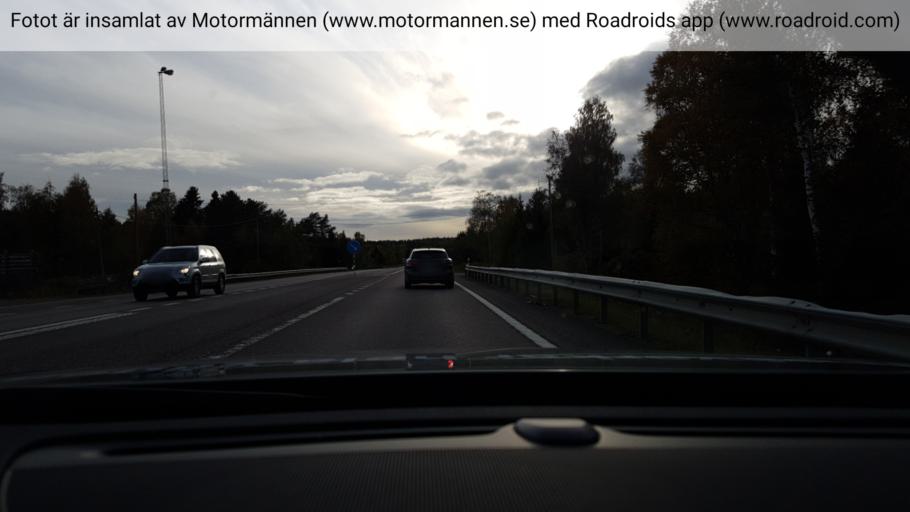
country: SE
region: Vaesternorrland
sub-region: Timra Kommun
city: Soraker
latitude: 62.5564
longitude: 17.6433
